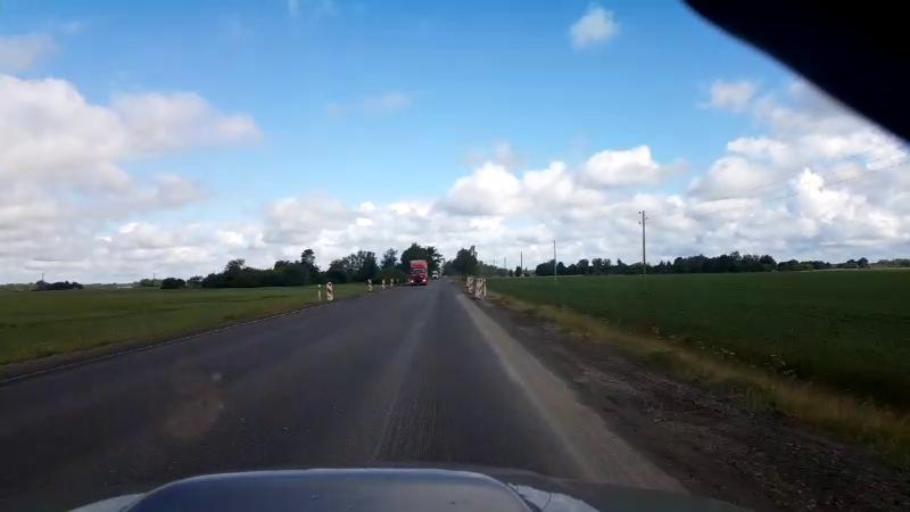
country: LV
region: Bauskas Rajons
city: Bauska
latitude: 56.3400
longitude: 24.2932
